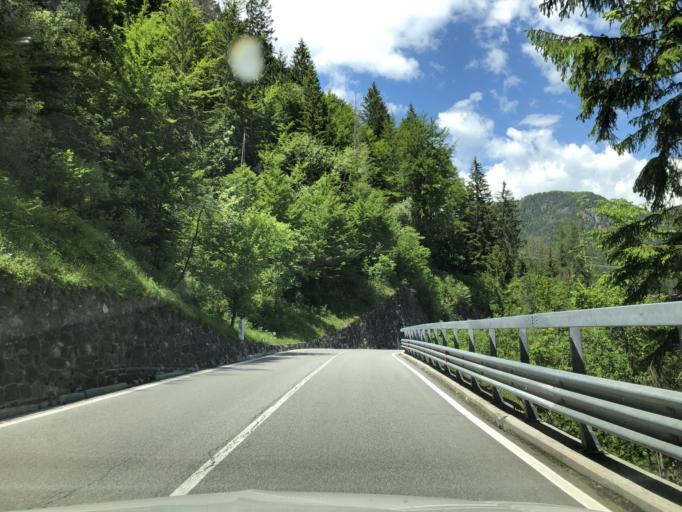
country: IT
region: Friuli Venezia Giulia
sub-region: Provincia di Udine
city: Tarvisio
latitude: 46.4937
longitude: 13.5862
